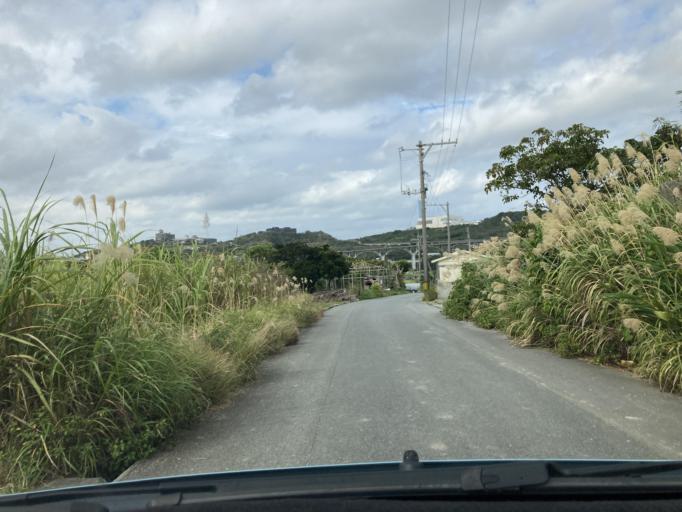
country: JP
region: Okinawa
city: Ginowan
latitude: 26.2093
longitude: 127.7443
